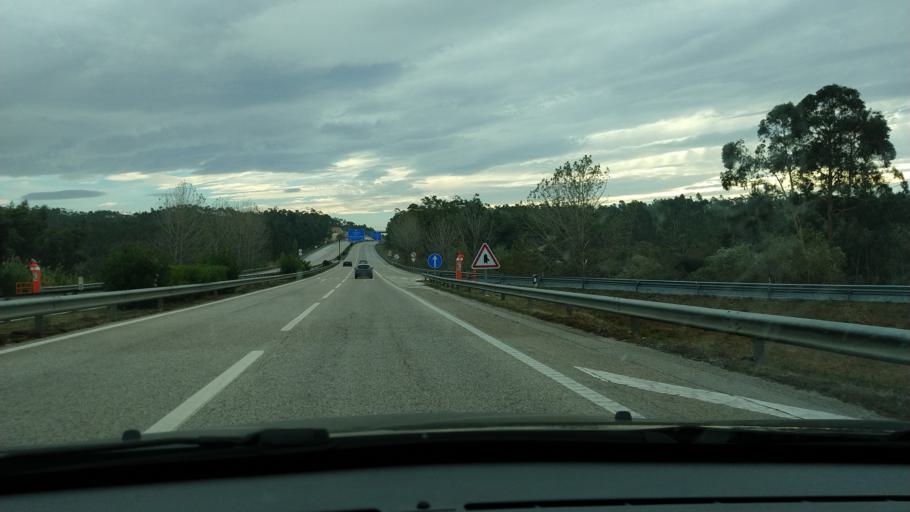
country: PT
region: Coimbra
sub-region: Figueira da Foz
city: Alhadas
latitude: 40.1537
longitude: -8.7933
